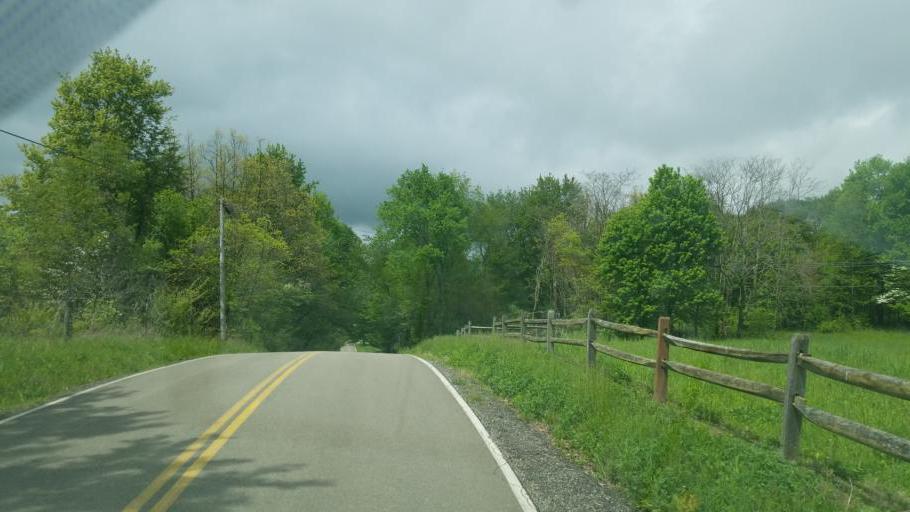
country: US
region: Ohio
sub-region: Tuscarawas County
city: Rockford
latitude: 40.4282
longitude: -81.2345
